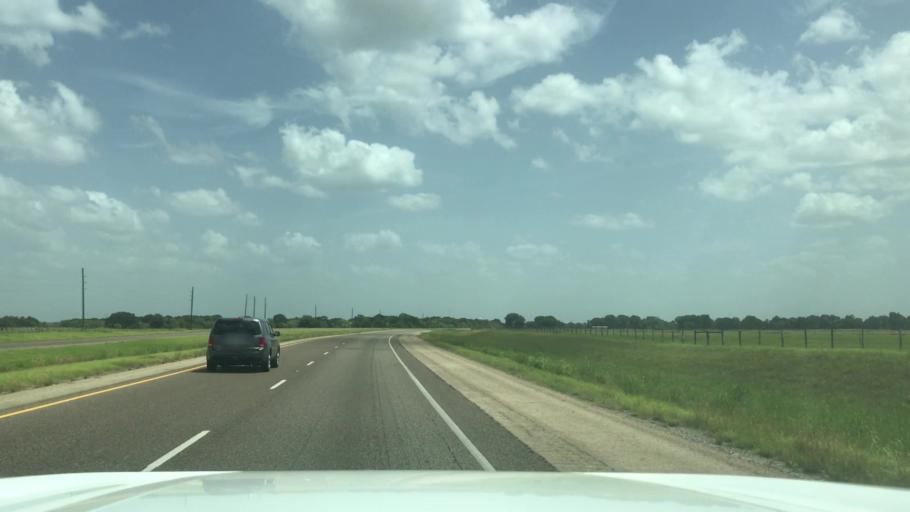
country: US
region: Texas
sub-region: Robertson County
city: Calvert
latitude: 31.0052
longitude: -96.6989
